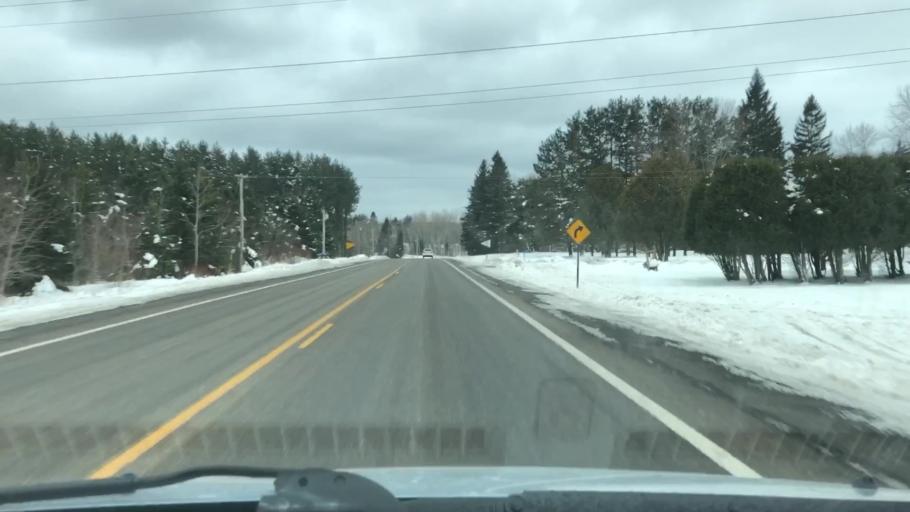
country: US
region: Minnesota
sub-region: Carlton County
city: Esko
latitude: 46.6795
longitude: -92.3723
